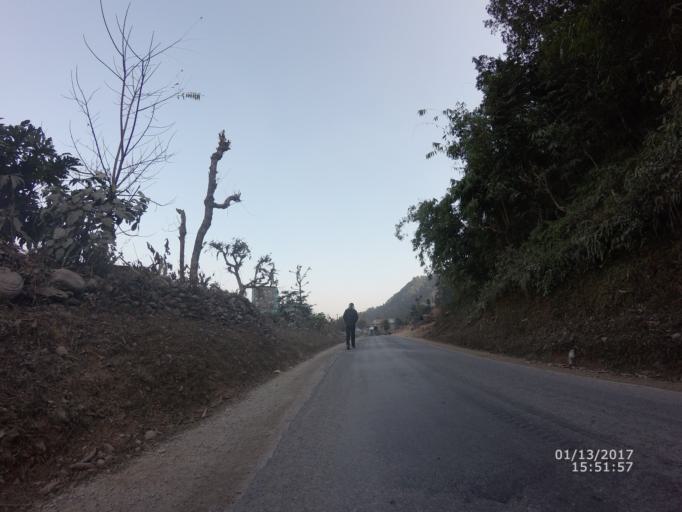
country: NP
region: Western Region
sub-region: Gandaki Zone
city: Pokhara
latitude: 28.1581
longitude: 84.0130
